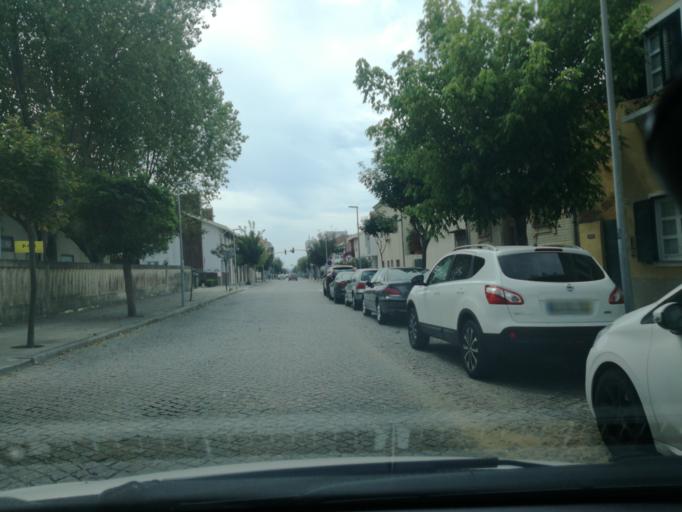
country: PT
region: Aveiro
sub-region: Espinho
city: Espinho
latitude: 41.0051
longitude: -8.6399
